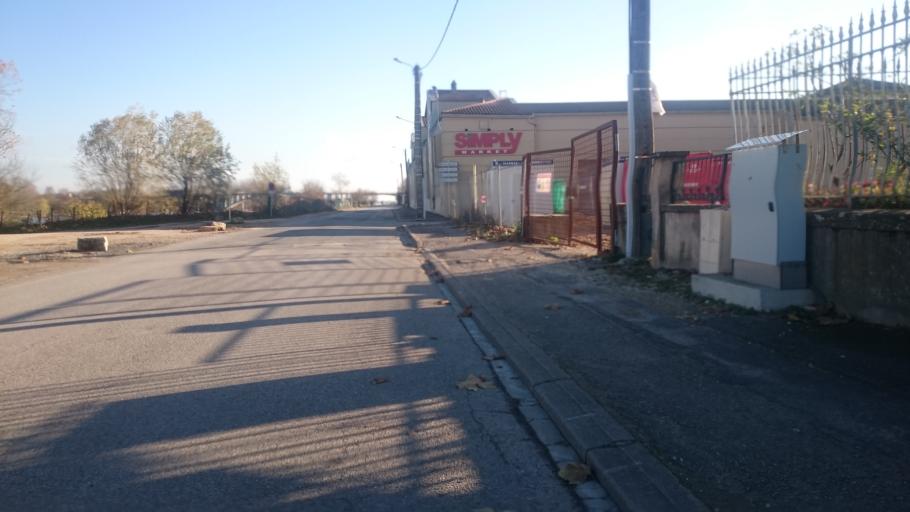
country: FR
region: Bourgogne
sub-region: Departement de Saone-et-Loire
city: Tournus
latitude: 46.5599
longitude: 4.9156
